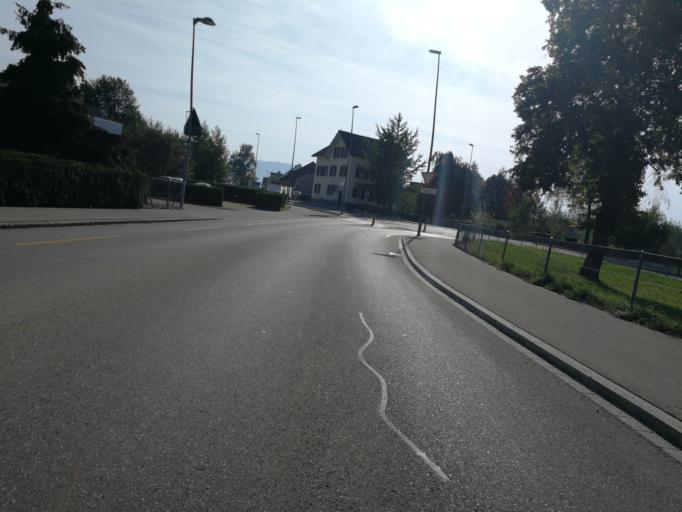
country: CH
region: Zurich
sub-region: Bezirk Hinwil
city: Tann
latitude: 47.2713
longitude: 8.8528
